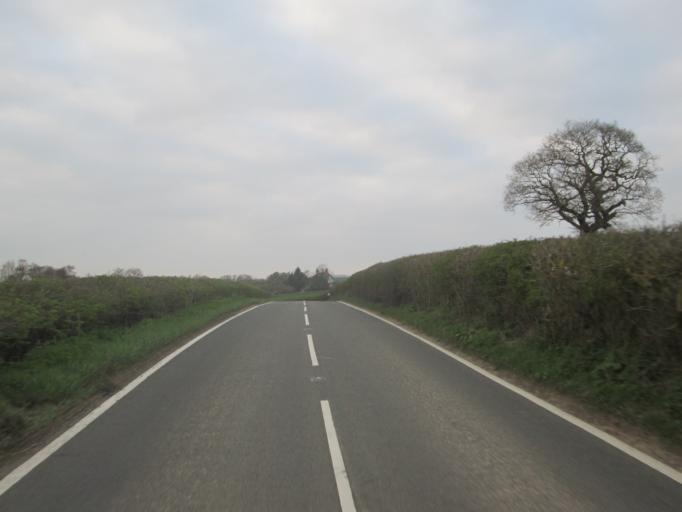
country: GB
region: England
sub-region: Derbyshire
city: Duffield
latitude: 53.0084
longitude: -1.5348
